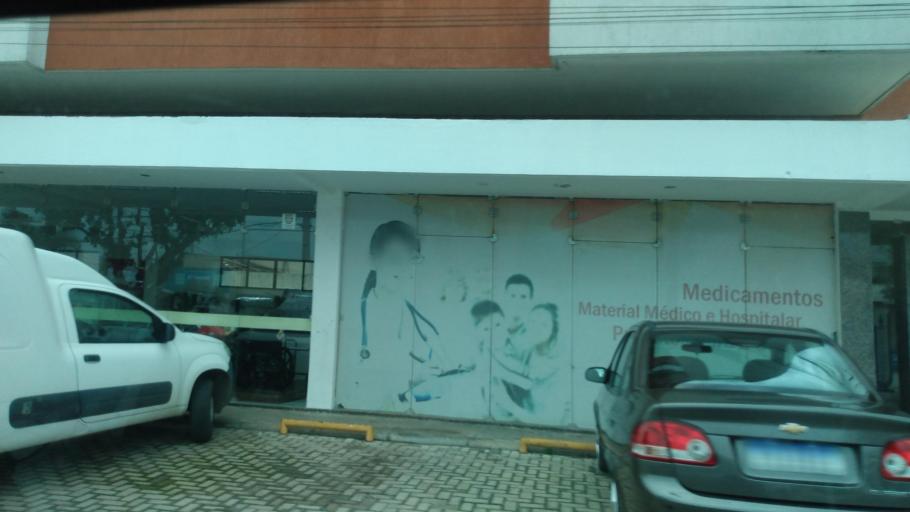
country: BR
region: Pernambuco
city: Garanhuns
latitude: -8.8843
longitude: -36.4782
